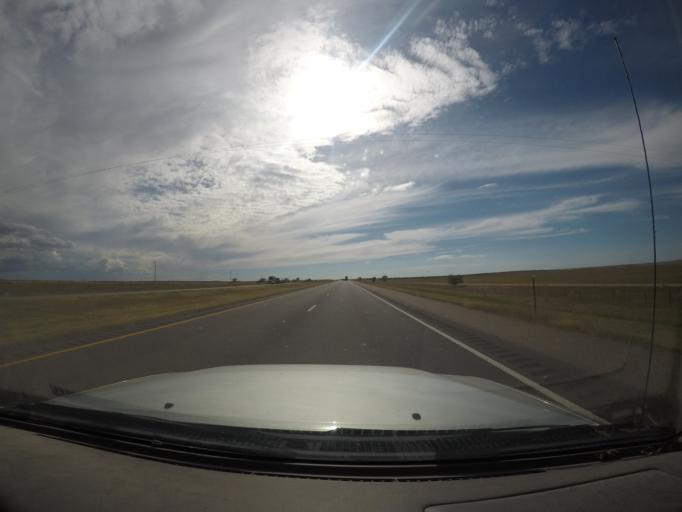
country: US
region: Nebraska
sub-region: Kimball County
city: Kimball
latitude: 41.1920
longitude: -103.8168
